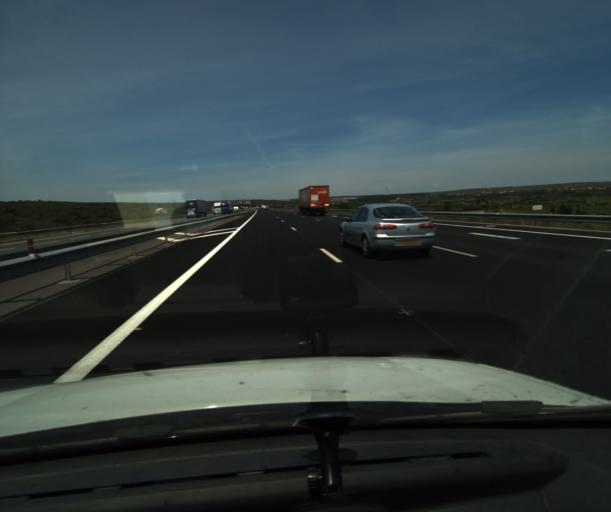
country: FR
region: Languedoc-Roussillon
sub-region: Departement de l'Aude
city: Leucate
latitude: 42.9545
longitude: 2.9705
